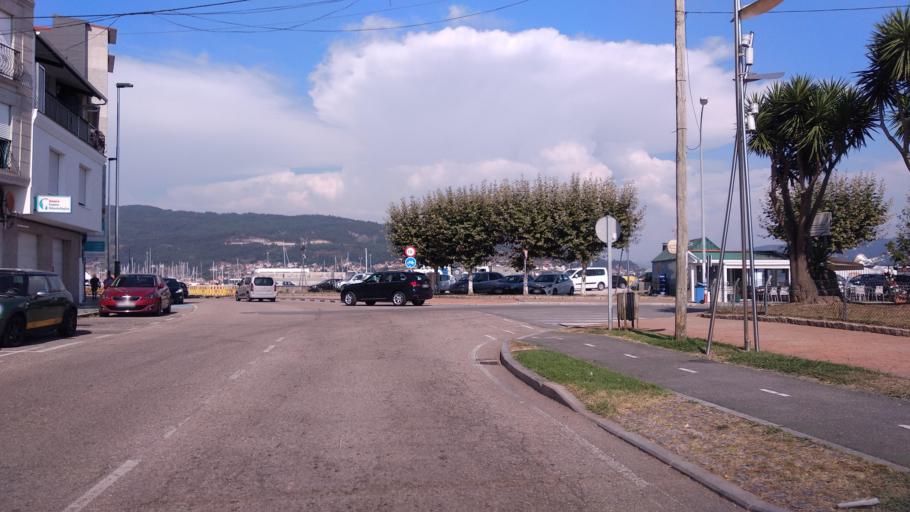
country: ES
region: Galicia
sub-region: Provincia de Pontevedra
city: Moana
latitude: 42.2743
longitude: -8.7373
